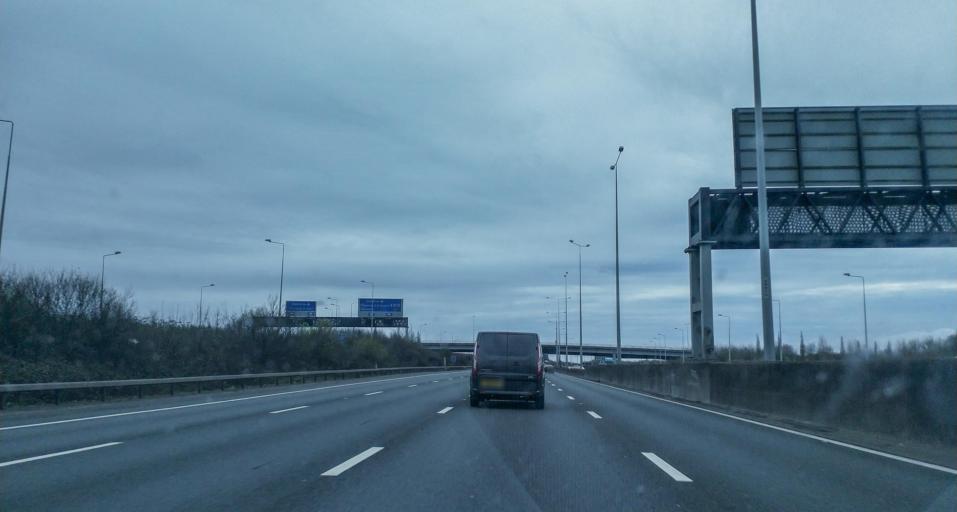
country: GB
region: England
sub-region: Surrey
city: Colnbrook
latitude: 51.4773
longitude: -0.5039
